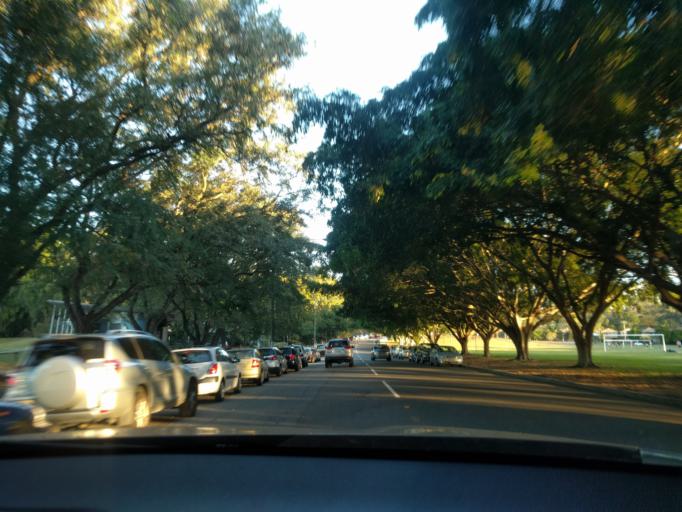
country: AU
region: Queensland
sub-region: Brisbane
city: South Brisbane
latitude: -27.4953
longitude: 153.0064
